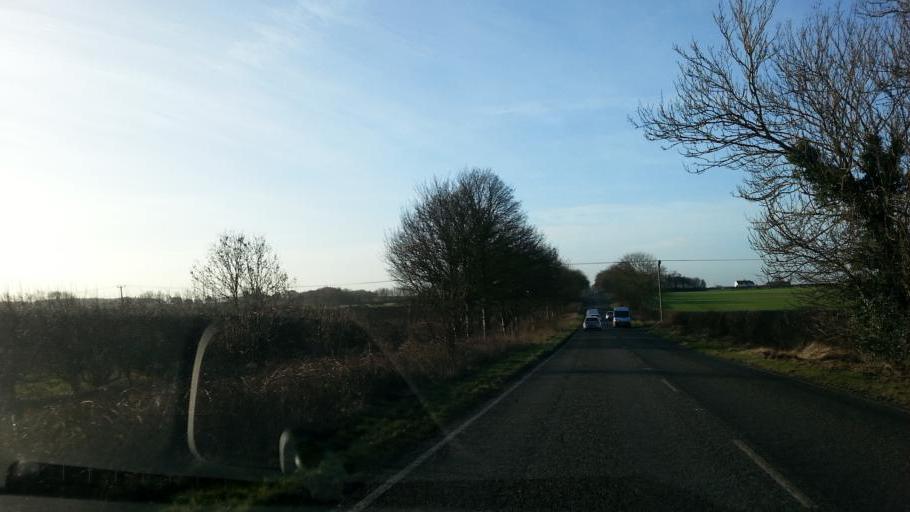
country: GB
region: England
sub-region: Lincolnshire
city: Grantham
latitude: 52.9220
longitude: -0.5751
